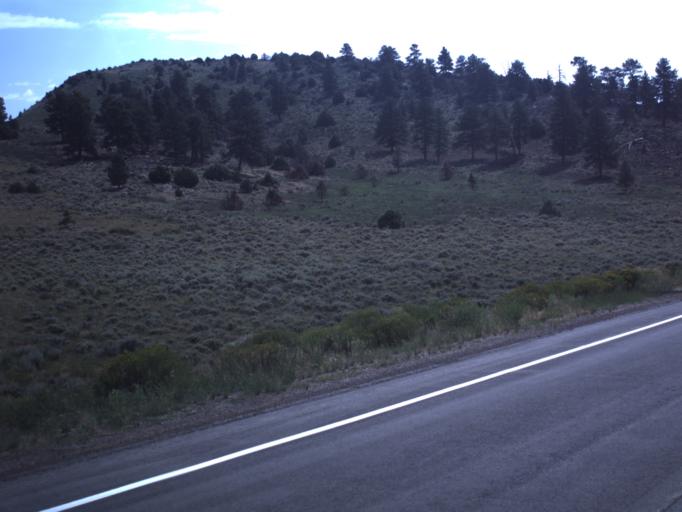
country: US
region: Utah
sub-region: Daggett County
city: Manila
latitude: 40.8872
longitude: -109.7040
